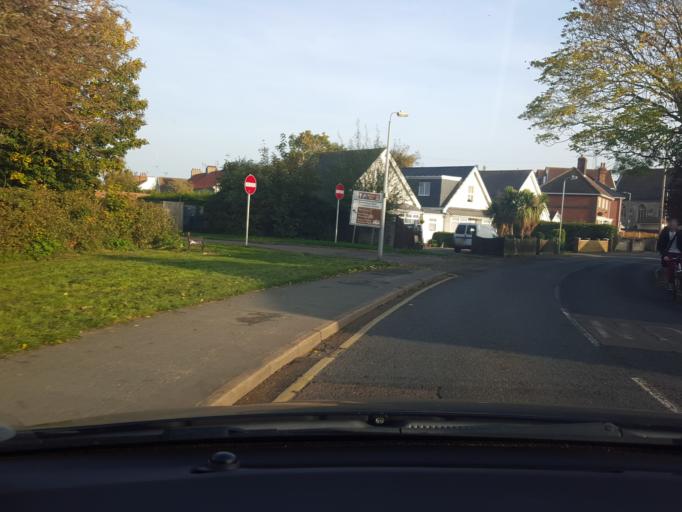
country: GB
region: England
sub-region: Essex
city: Walton-on-the-Naze
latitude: 51.8490
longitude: 1.2667
